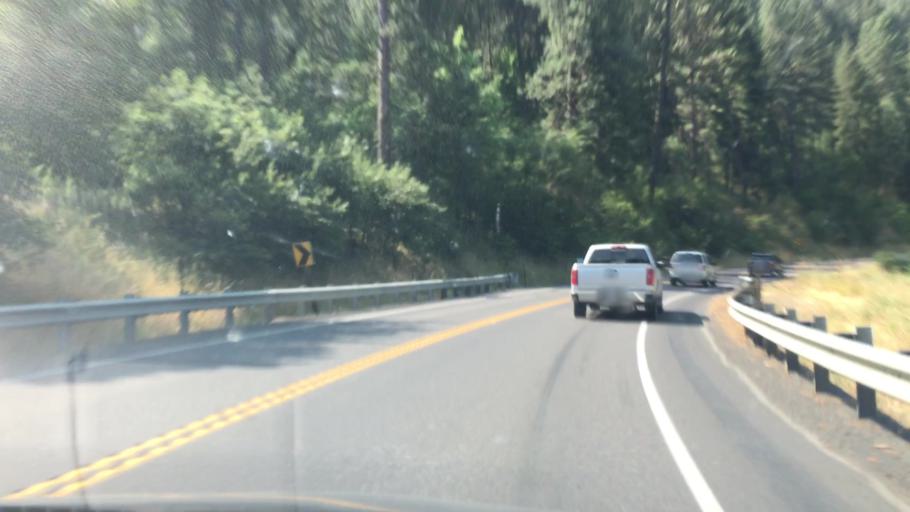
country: US
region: Idaho
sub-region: Clearwater County
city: Orofino
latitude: 46.4904
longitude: -116.4500
